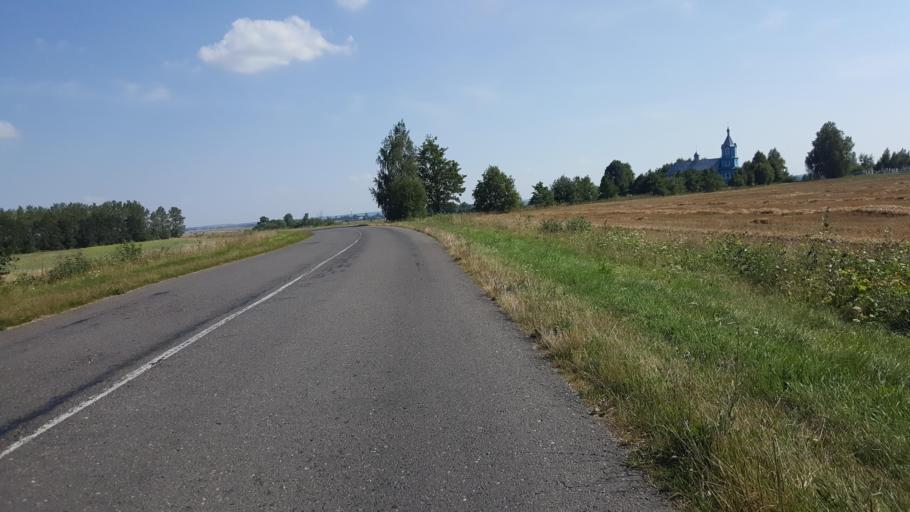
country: BY
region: Brest
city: Kamyanyets
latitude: 52.4475
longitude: 23.7330
